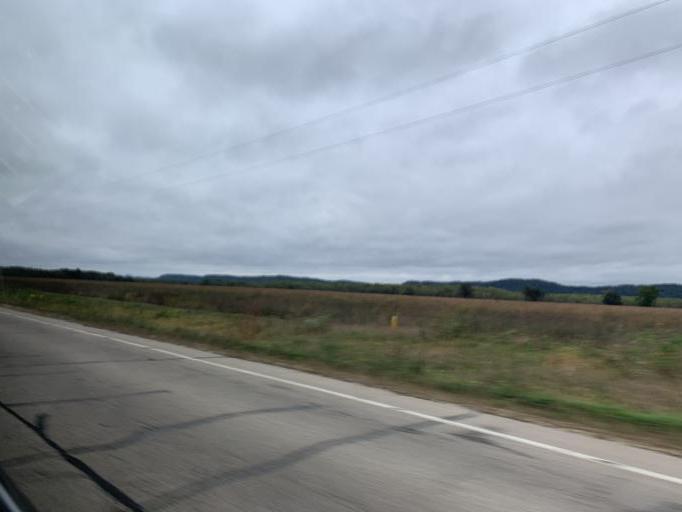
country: US
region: Wisconsin
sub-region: Grant County
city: Boscobel
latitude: 43.2053
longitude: -90.6020
